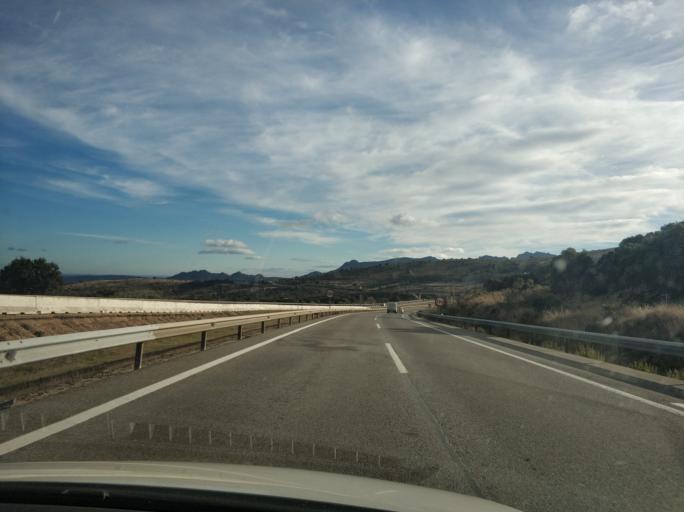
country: ES
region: Madrid
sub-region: Provincia de Madrid
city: Buitrago del Lozoya
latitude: 40.9535
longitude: -3.6402
